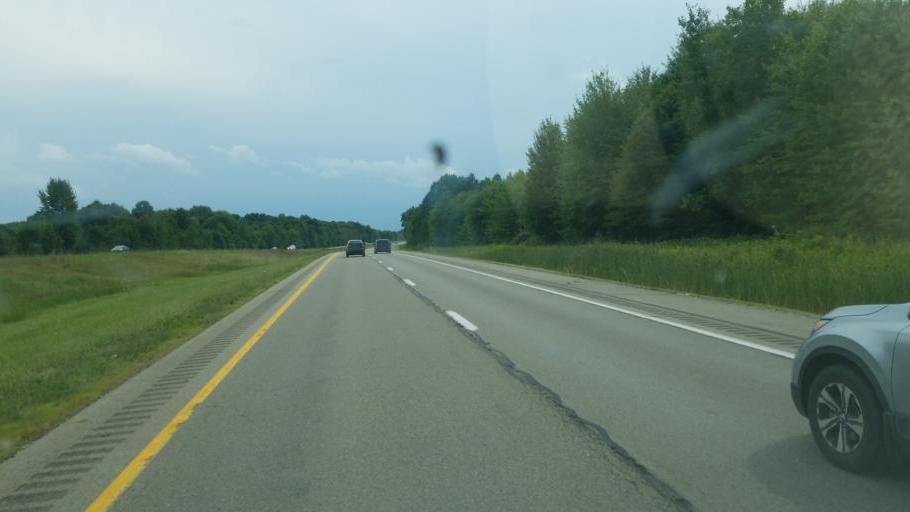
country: US
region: Pennsylvania
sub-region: Crawford County
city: Cochranton
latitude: 41.5005
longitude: -80.1688
